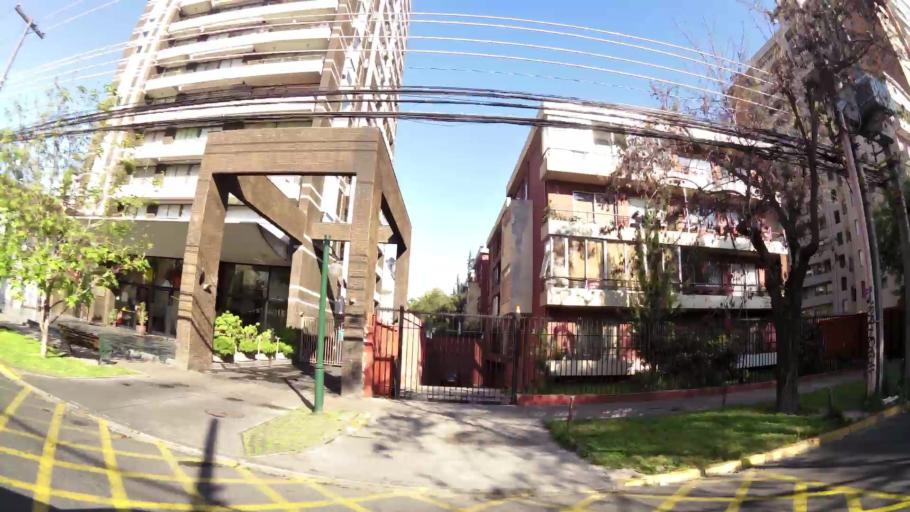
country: CL
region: Santiago Metropolitan
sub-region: Provincia de Santiago
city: Villa Presidente Frei, Nunoa, Santiago, Chile
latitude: -33.4547
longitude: -70.5919
